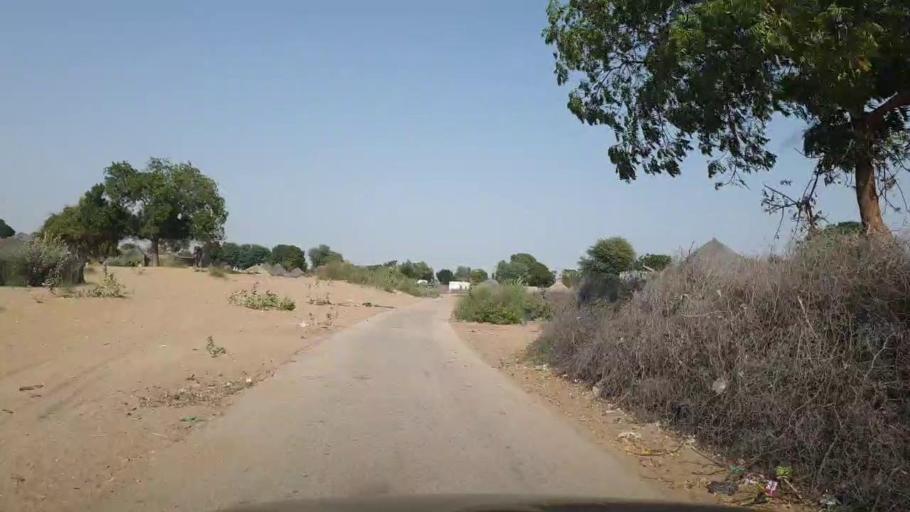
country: PK
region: Sindh
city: Islamkot
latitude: 25.1326
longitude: 70.4575
